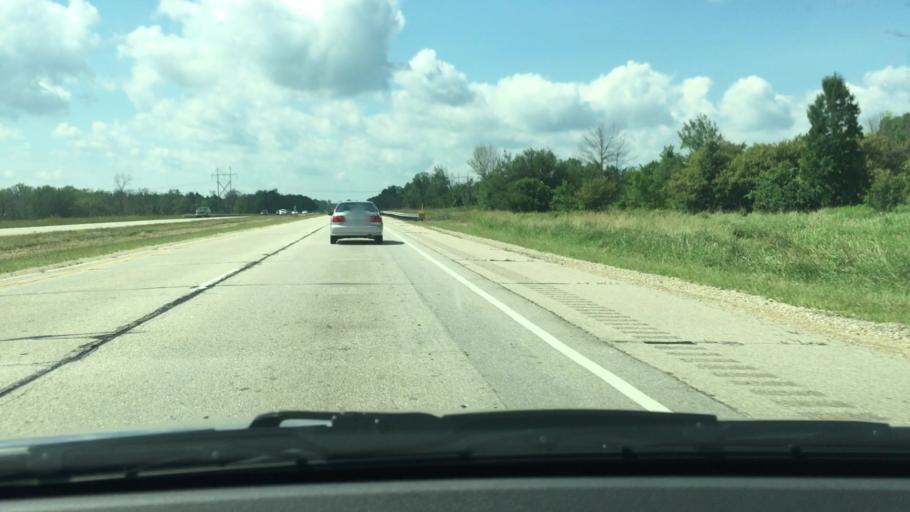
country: US
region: Wisconsin
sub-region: Dodge County
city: Theresa
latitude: 43.4458
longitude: -88.3531
